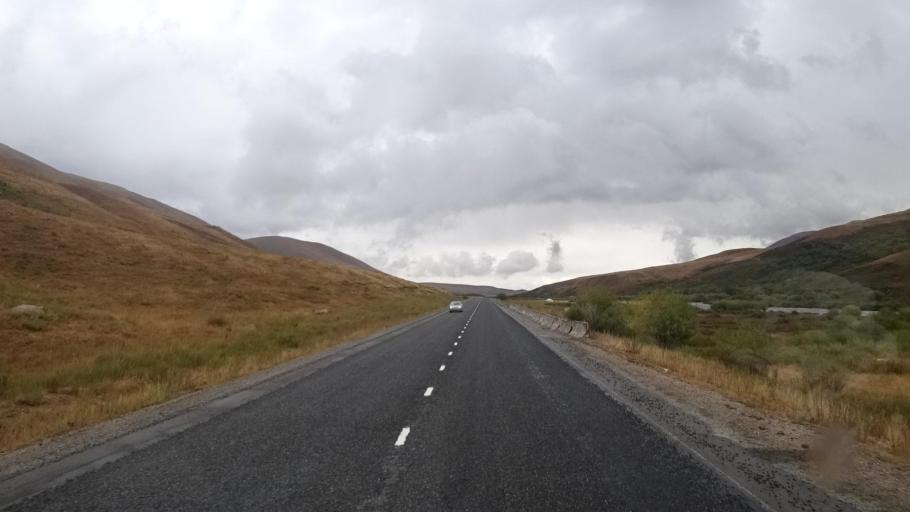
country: KG
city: Sosnovka
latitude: 42.2031
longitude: 73.6007
